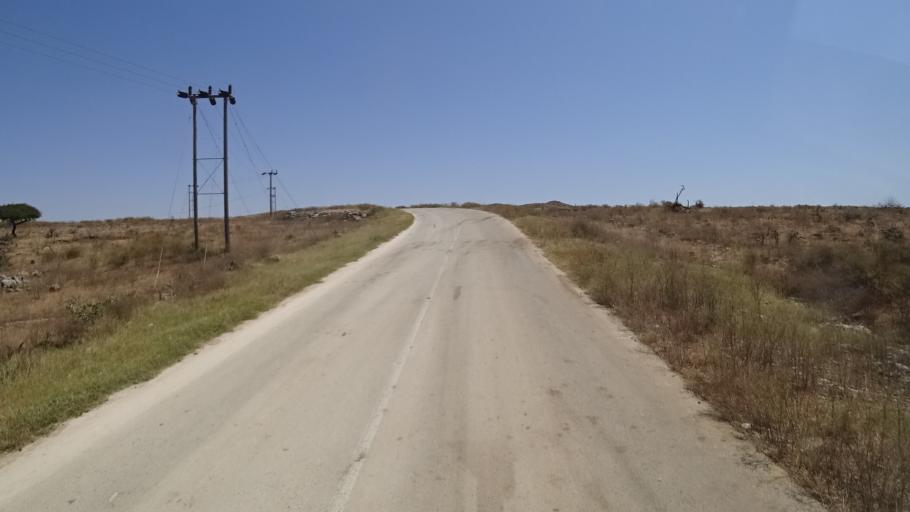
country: OM
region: Zufar
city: Salalah
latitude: 17.1475
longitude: 54.6161
